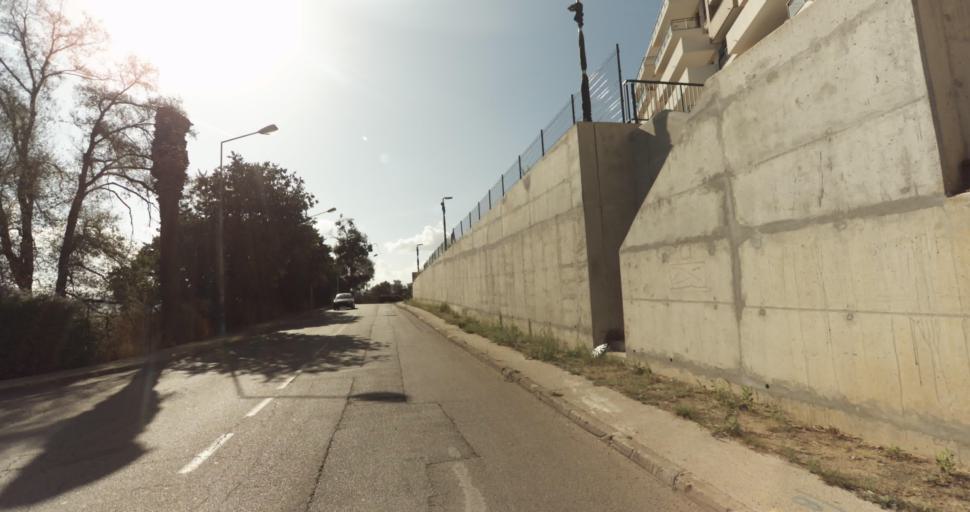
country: FR
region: Corsica
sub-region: Departement de la Corse-du-Sud
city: Ajaccio
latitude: 41.9242
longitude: 8.7298
